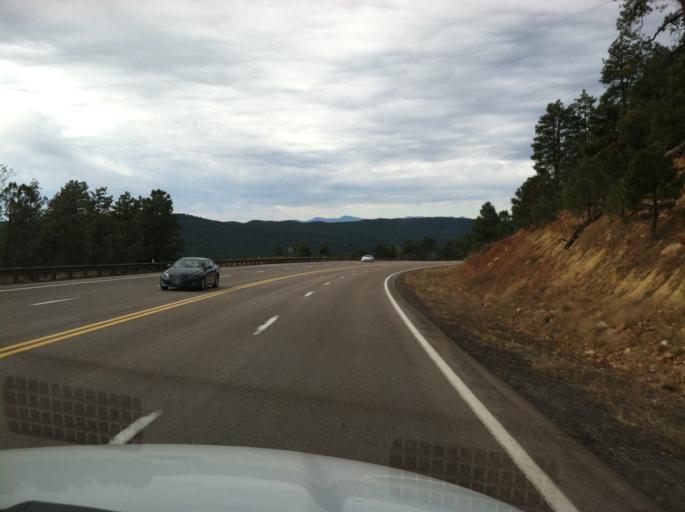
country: US
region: Arizona
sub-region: Gila County
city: Star Valley
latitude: 34.3059
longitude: -110.9363
